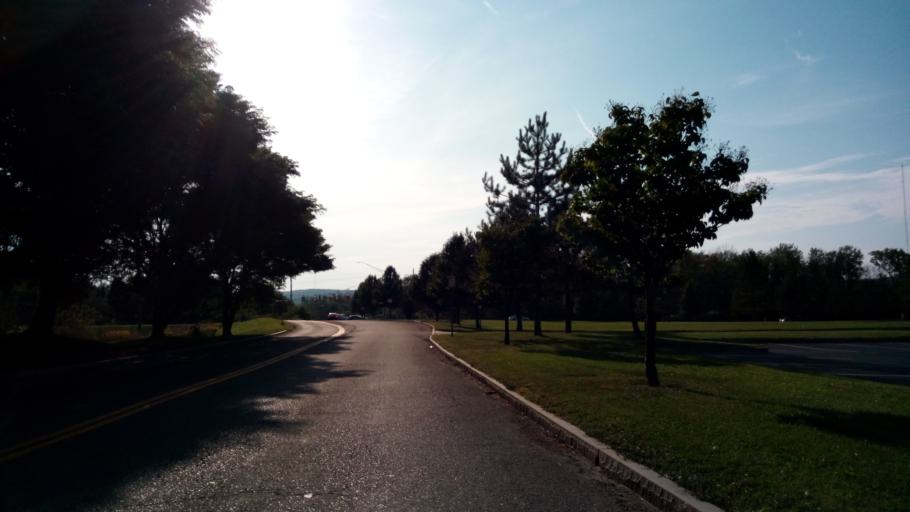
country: US
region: New York
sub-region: Chemung County
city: Elmira Heights
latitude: 42.1175
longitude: -76.8066
